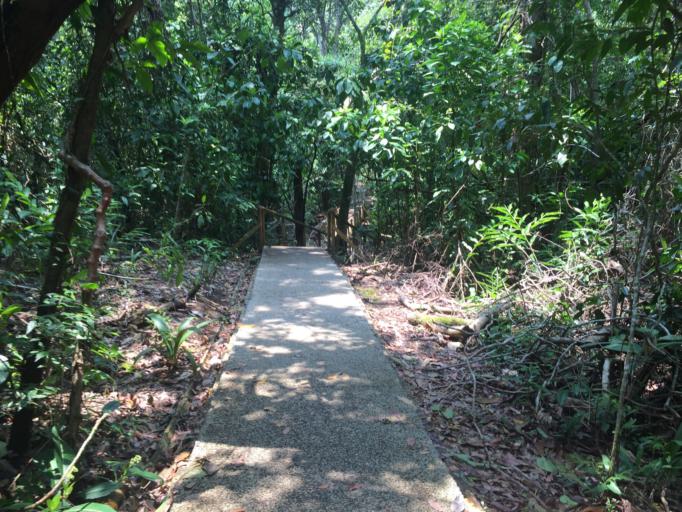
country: CR
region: Puntarenas
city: Quepos
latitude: 9.3827
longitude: -84.1423
